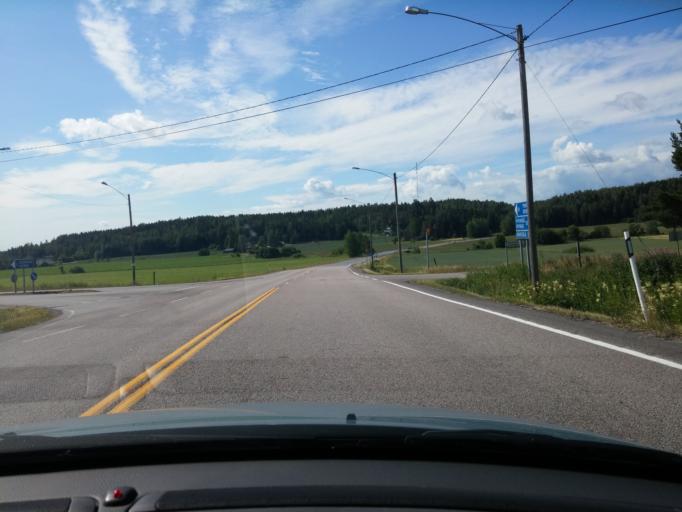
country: FI
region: Uusimaa
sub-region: Porvoo
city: Askola
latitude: 60.4462
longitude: 25.5856
